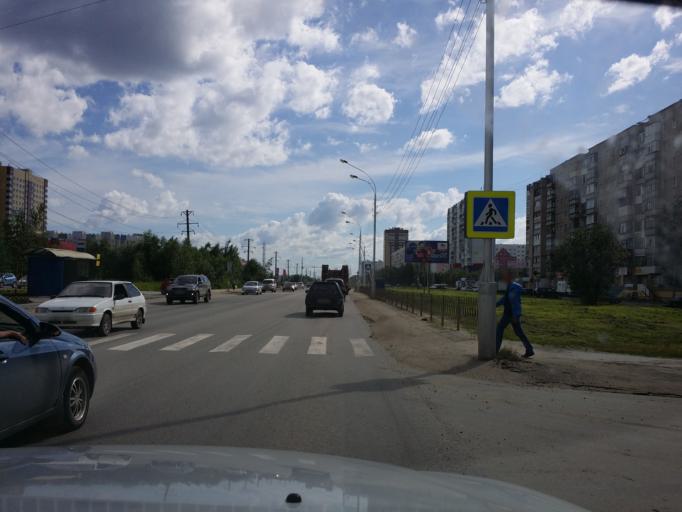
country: RU
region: Khanty-Mansiyskiy Avtonomnyy Okrug
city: Nizhnevartovsk
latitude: 60.9319
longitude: 76.6097
